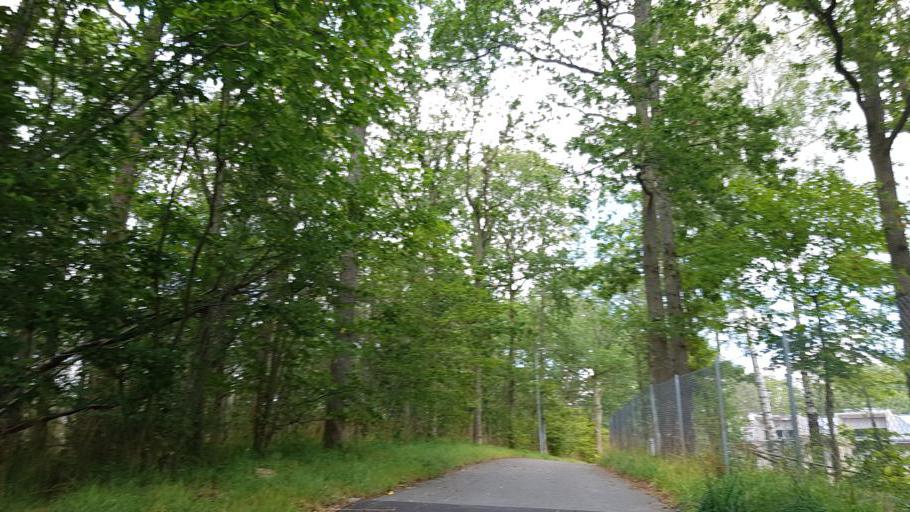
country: SE
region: Vaestra Goetaland
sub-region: Harryda Kommun
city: Molnlycke
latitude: 57.6657
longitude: 12.0978
